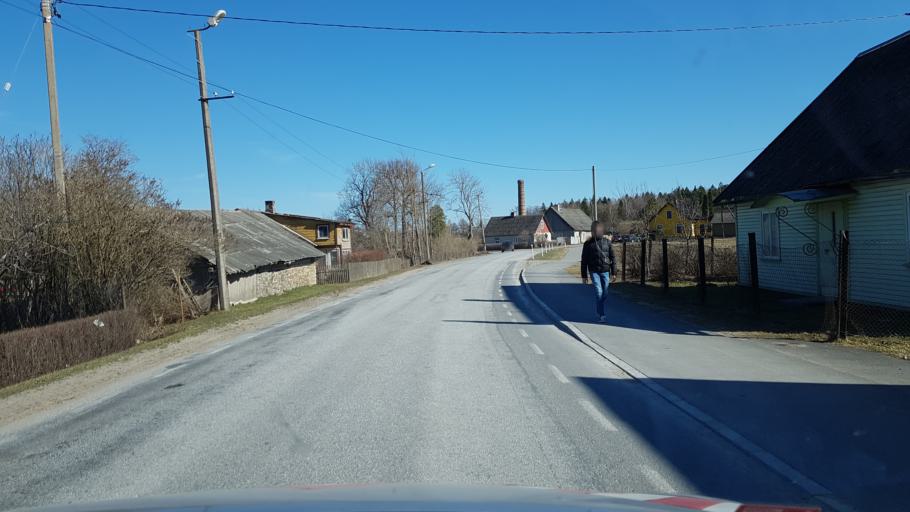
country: EE
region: Laeaene-Virumaa
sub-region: Rakke vald
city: Rakke
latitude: 58.9855
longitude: 26.2508
